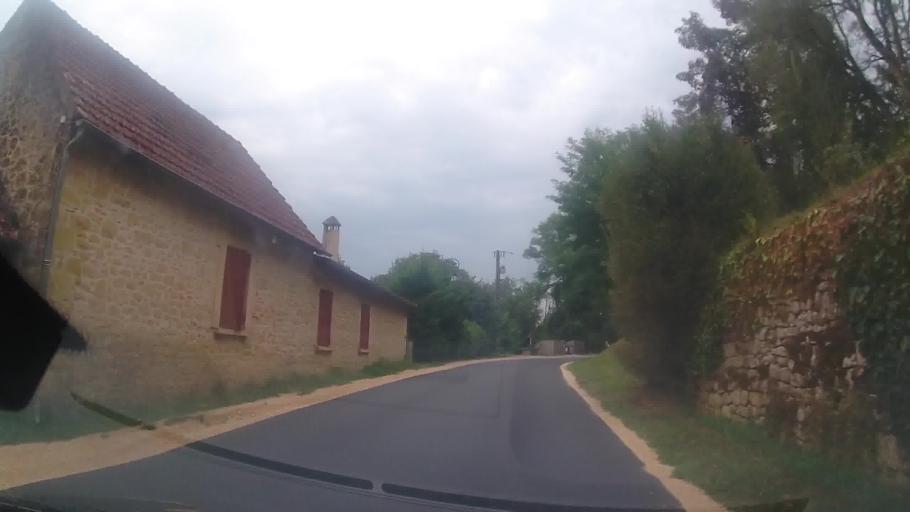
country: FR
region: Aquitaine
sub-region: Departement de la Dordogne
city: Carsac-Aillac
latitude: 44.8413
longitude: 1.3014
